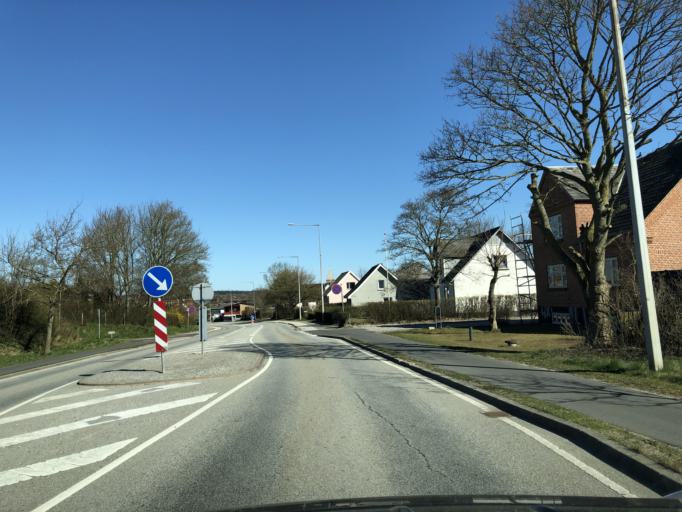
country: DK
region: North Denmark
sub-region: Rebild Kommune
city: Stovring
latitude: 56.8819
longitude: 9.8398
